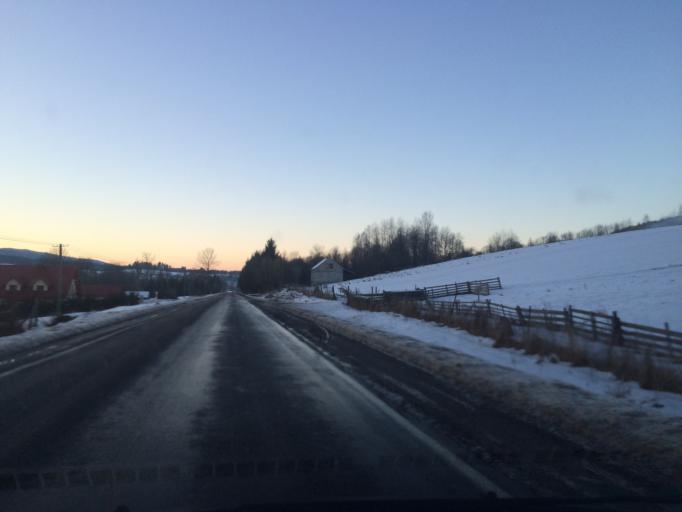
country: PL
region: Subcarpathian Voivodeship
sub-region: Powiat bieszczadzki
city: Czarna
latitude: 49.3694
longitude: 22.6543
